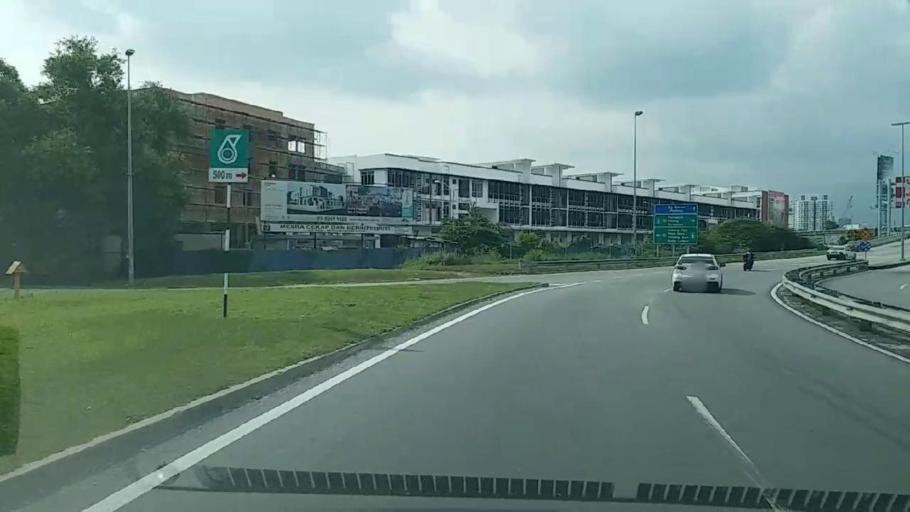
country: MY
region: Selangor
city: Subang Jaya
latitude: 2.9896
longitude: 101.6180
